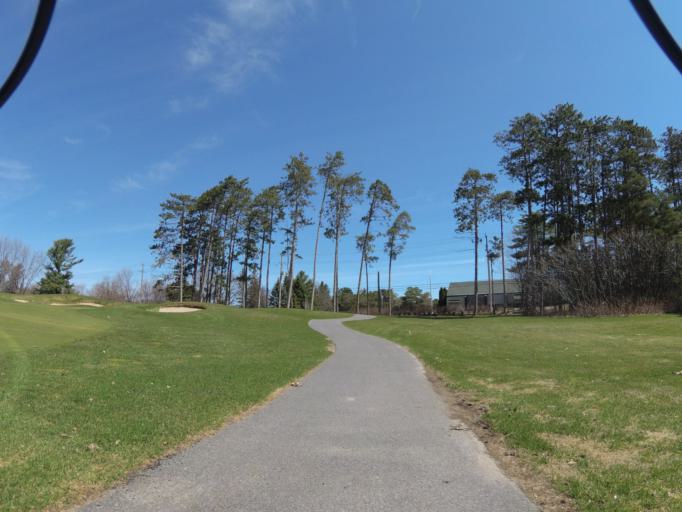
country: CA
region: Ontario
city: Ottawa
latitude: 45.3375
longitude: -75.6905
